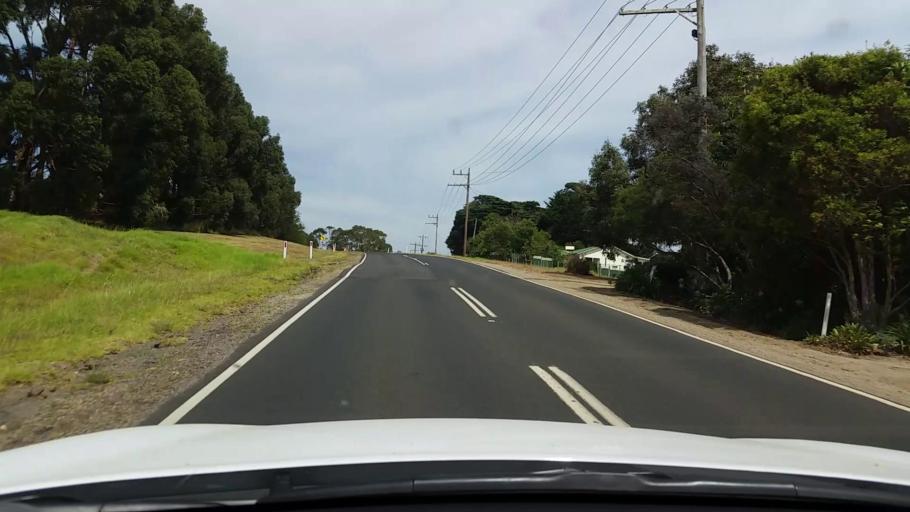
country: AU
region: Victoria
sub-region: Mornington Peninsula
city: Merricks
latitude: -38.4503
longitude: 145.0241
